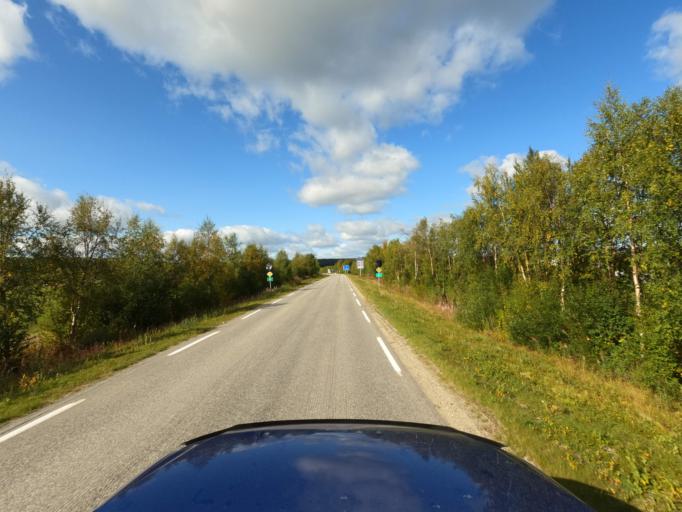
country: NO
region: Finnmark Fylke
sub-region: Karasjok
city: Karasjohka
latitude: 69.3987
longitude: 25.8381
